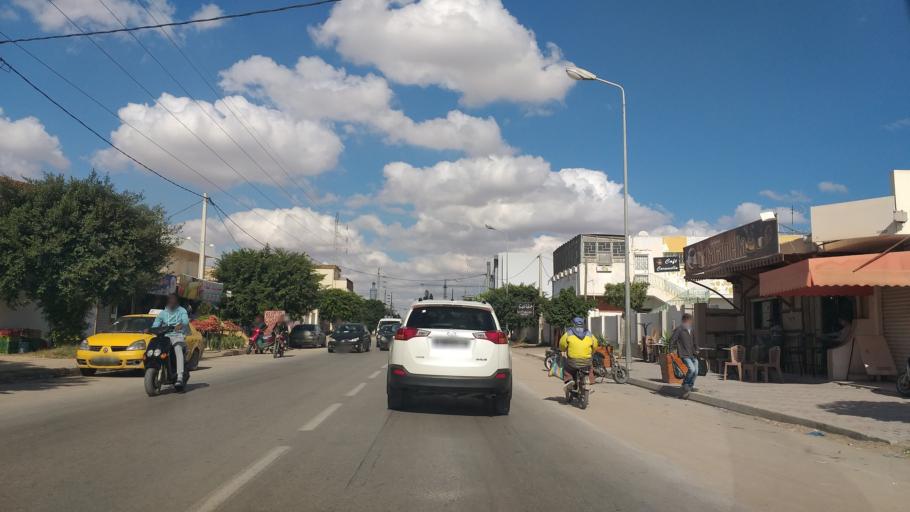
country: TN
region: Safaqis
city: Al Qarmadah
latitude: 34.7757
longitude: 10.7767
